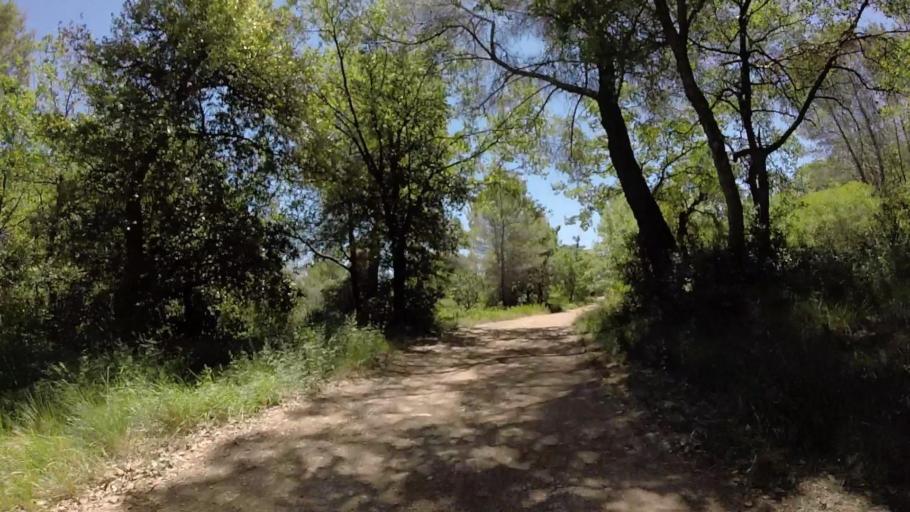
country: FR
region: Provence-Alpes-Cote d'Azur
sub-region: Departement des Alpes-Maritimes
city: Valbonne
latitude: 43.6338
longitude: 7.0335
